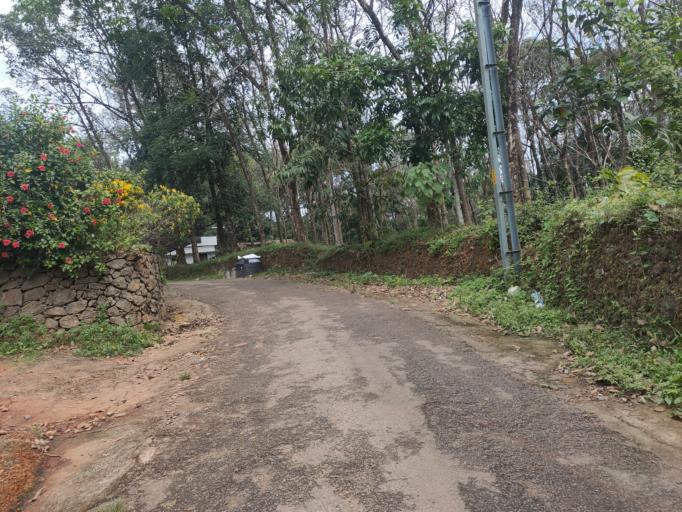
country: IN
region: Kerala
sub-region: Ernakulam
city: Kotamangalam
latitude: 10.0106
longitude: 76.6464
